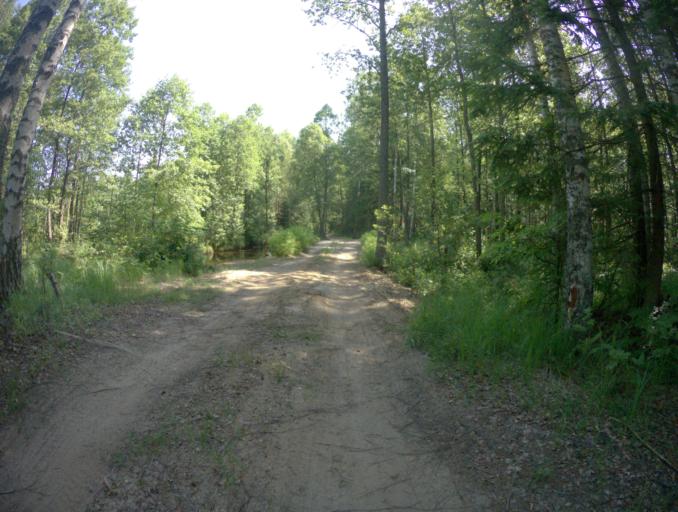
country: RU
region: Vladimir
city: Vyazniki
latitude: 56.3832
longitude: 42.2142
